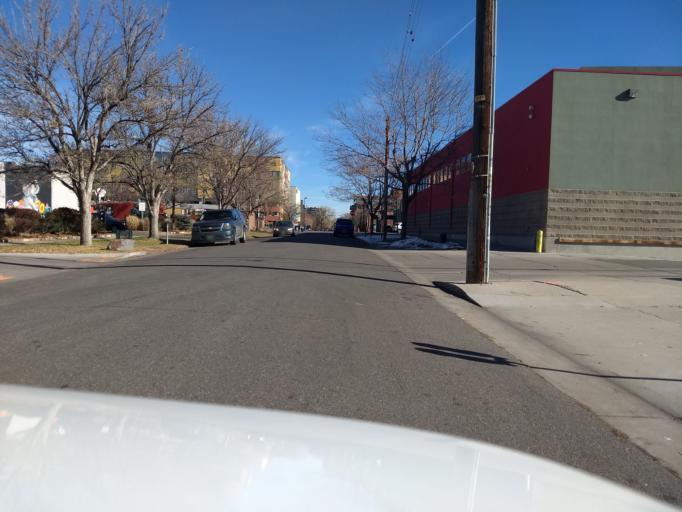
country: US
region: Colorado
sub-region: Denver County
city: Denver
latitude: 39.7241
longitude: -104.9886
